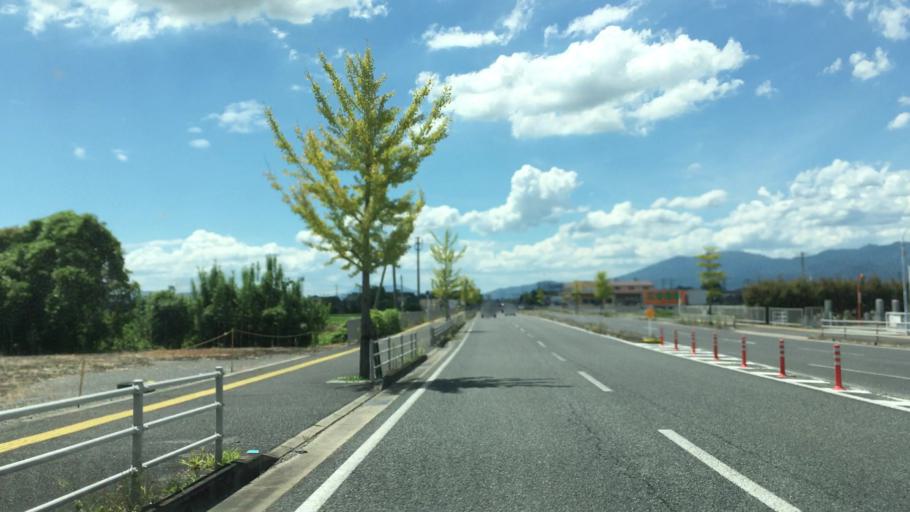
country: JP
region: Saga Prefecture
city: Saga-shi
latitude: 33.2744
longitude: 130.3292
